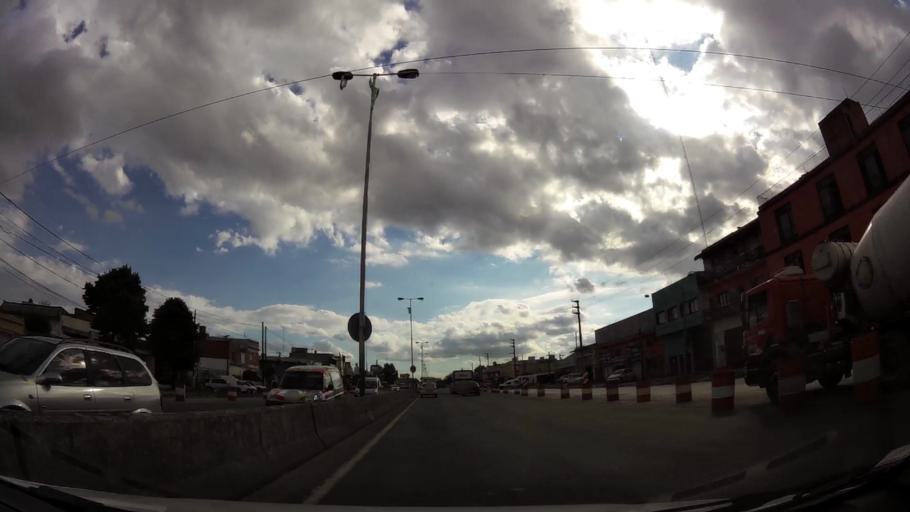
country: AR
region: Buenos Aires
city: San Justo
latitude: -34.6873
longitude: -58.5637
